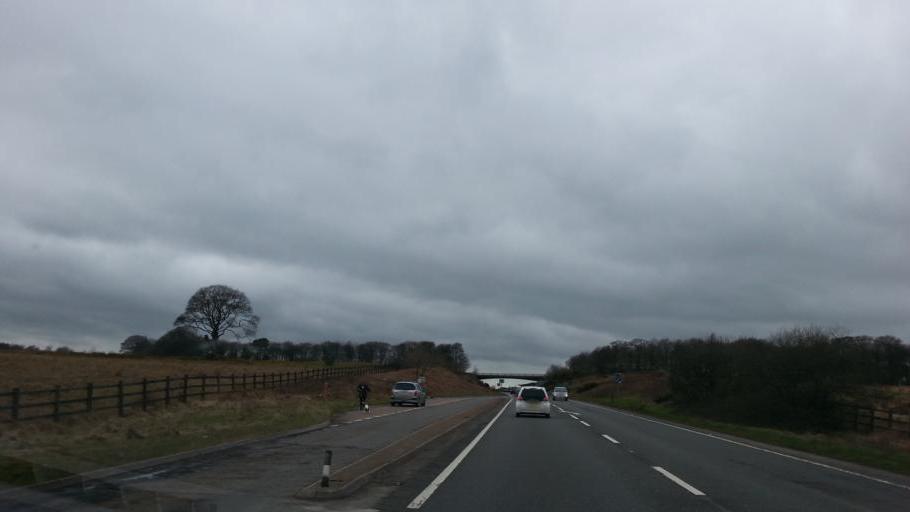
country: GB
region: England
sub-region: Devon
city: Tiverton
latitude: 50.9765
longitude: -3.6332
